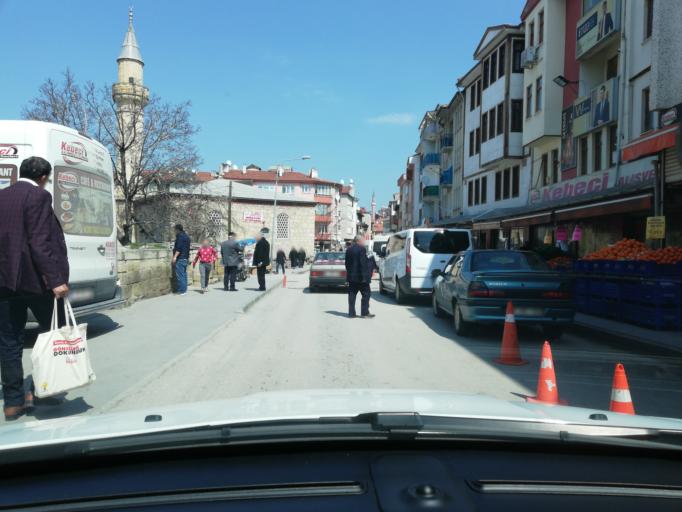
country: TR
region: Kastamonu
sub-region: Cide
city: Kastamonu
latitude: 41.3776
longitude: 33.7789
